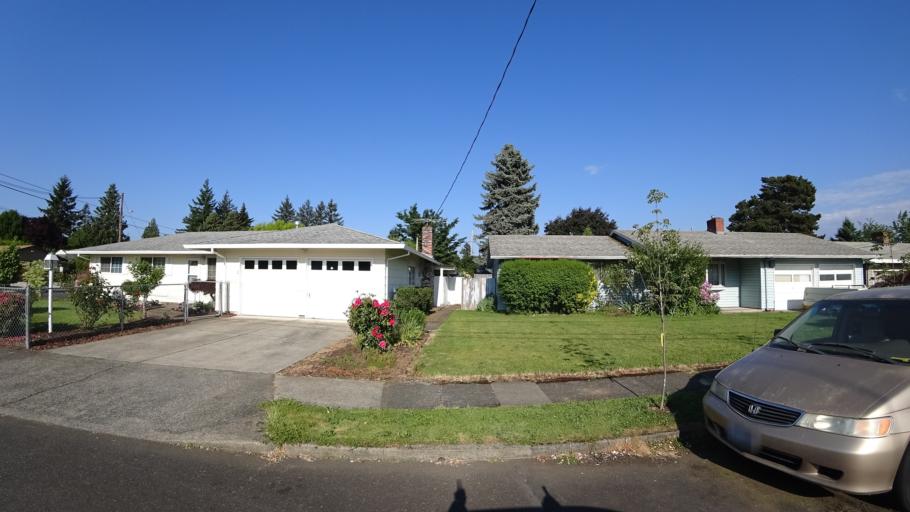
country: US
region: Oregon
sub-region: Multnomah County
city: Lents
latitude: 45.5176
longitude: -122.5063
